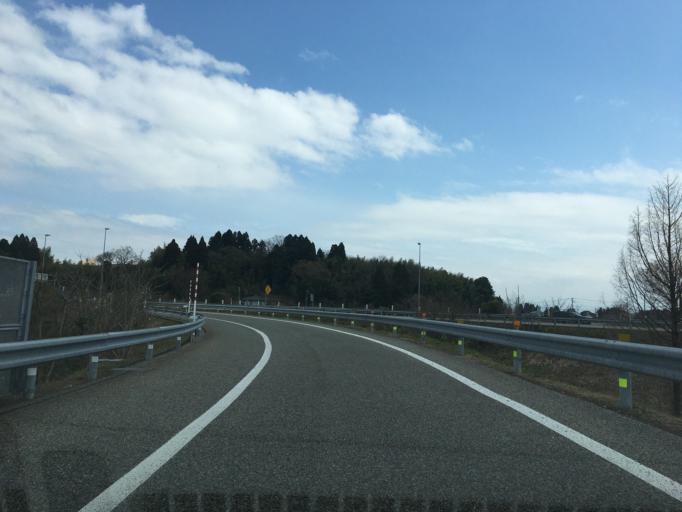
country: JP
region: Toyama
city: Kuragaki-kosugi
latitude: 36.6816
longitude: 137.1338
